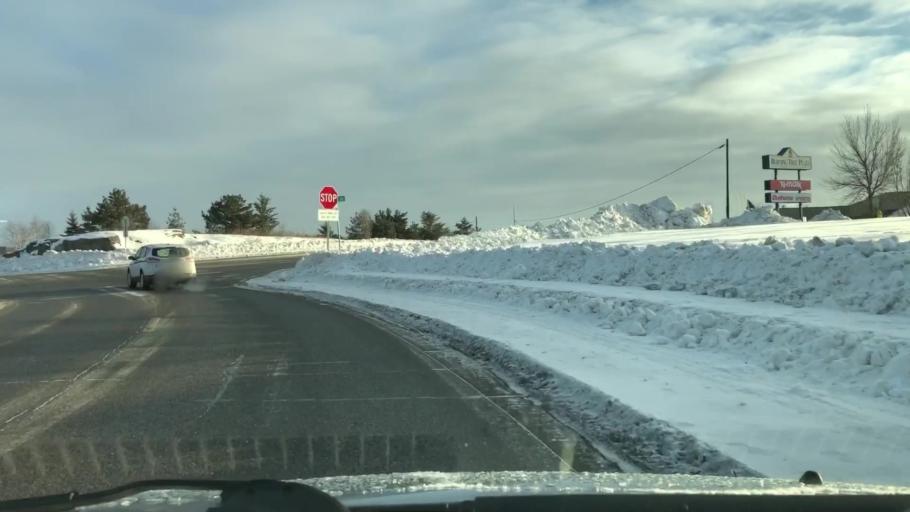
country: US
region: Minnesota
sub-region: Saint Louis County
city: Duluth
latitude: 46.8105
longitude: -92.1695
